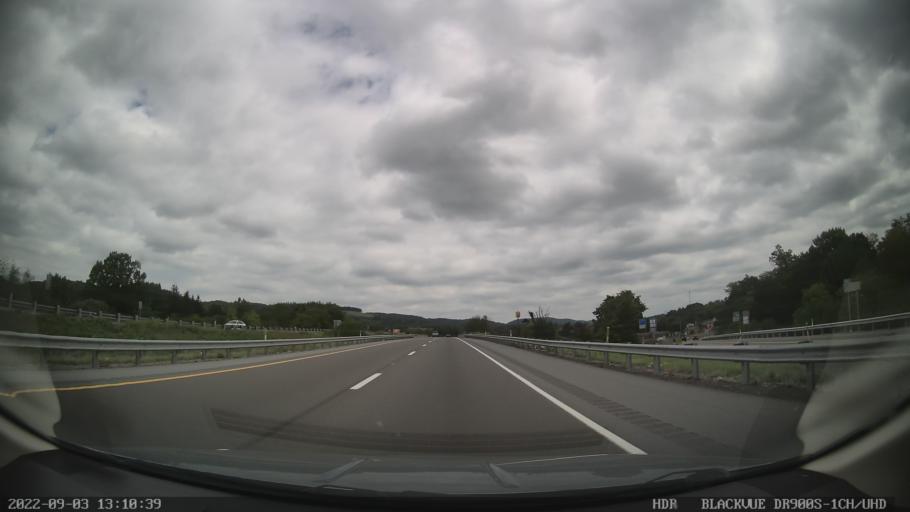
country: US
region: Pennsylvania
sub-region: Northumberland County
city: Riverside
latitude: 40.9953
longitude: -76.6461
